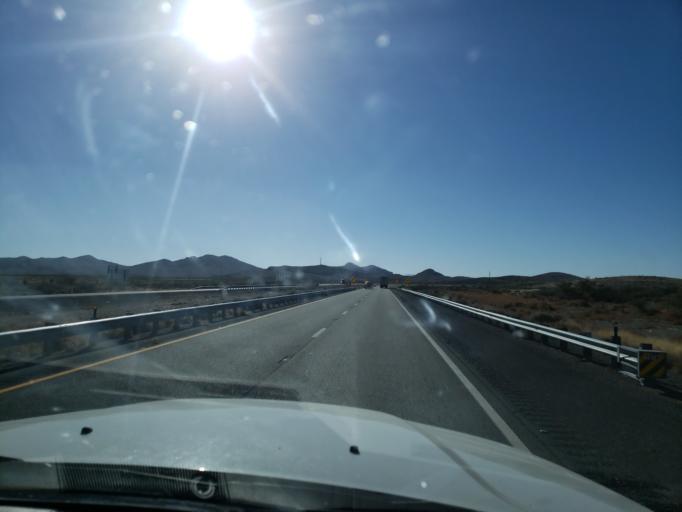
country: US
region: New Mexico
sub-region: Hidalgo County
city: Lordsburg
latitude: 32.2302
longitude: -108.9673
